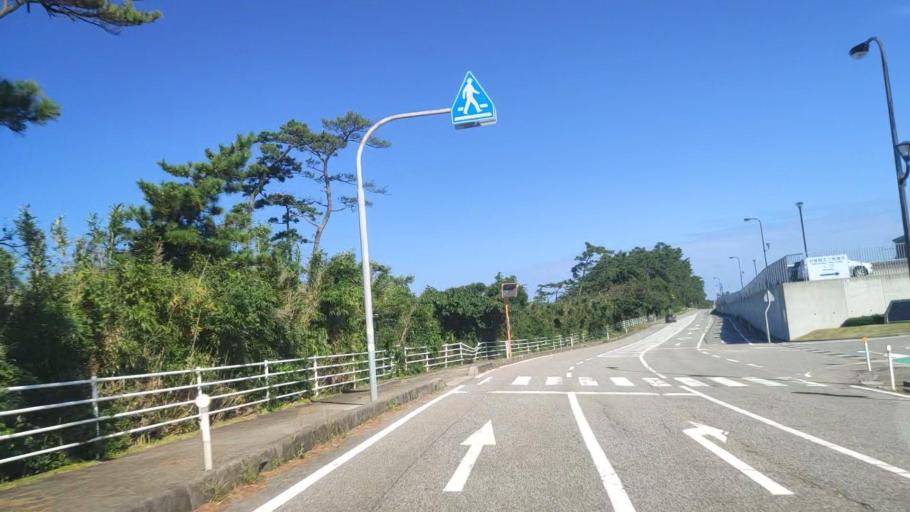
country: JP
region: Ishikawa
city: Hakui
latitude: 37.0558
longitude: 136.7242
